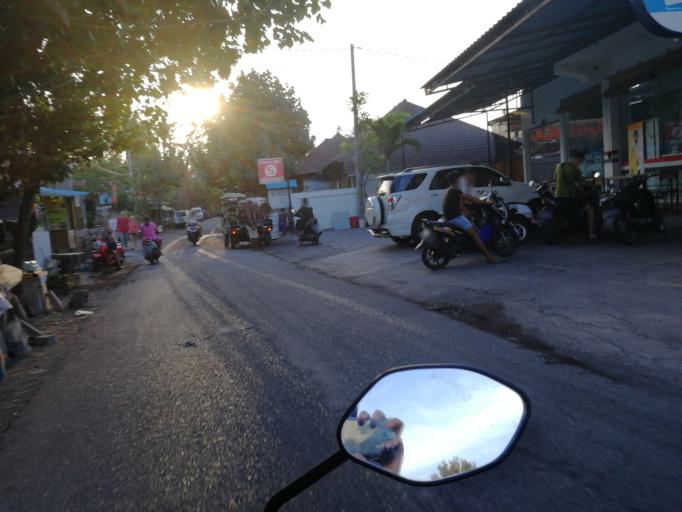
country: ID
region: Bali
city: Biaslantang Kaler
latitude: -8.3357
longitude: 115.6510
